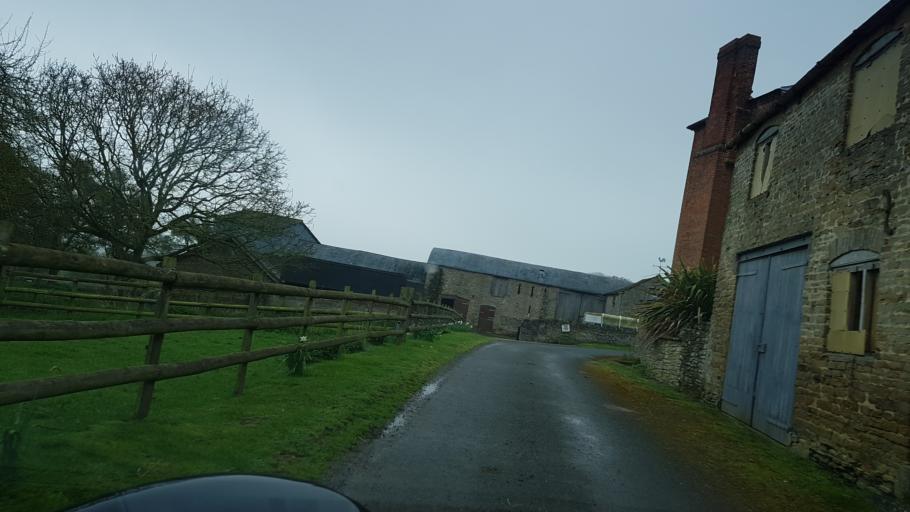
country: GB
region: England
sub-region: Herefordshire
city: Yatton
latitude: 52.0180
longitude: -2.5308
